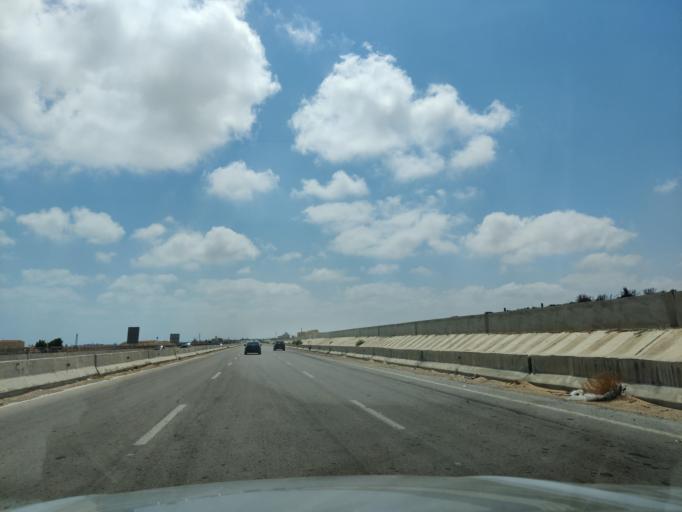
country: EG
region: Muhafazat Matruh
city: Al `Alamayn
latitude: 30.8216
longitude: 29.0049
